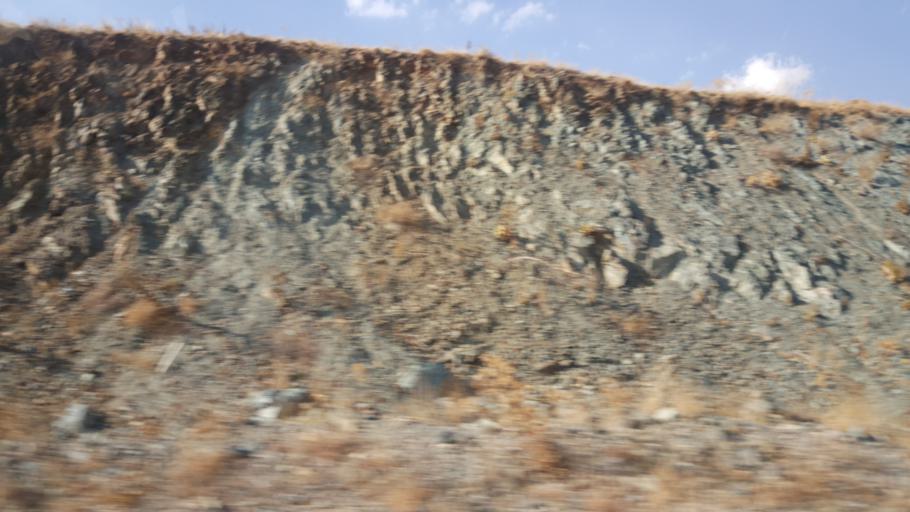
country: TR
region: Eskisehir
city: Kirka
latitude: 39.3286
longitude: 30.5772
